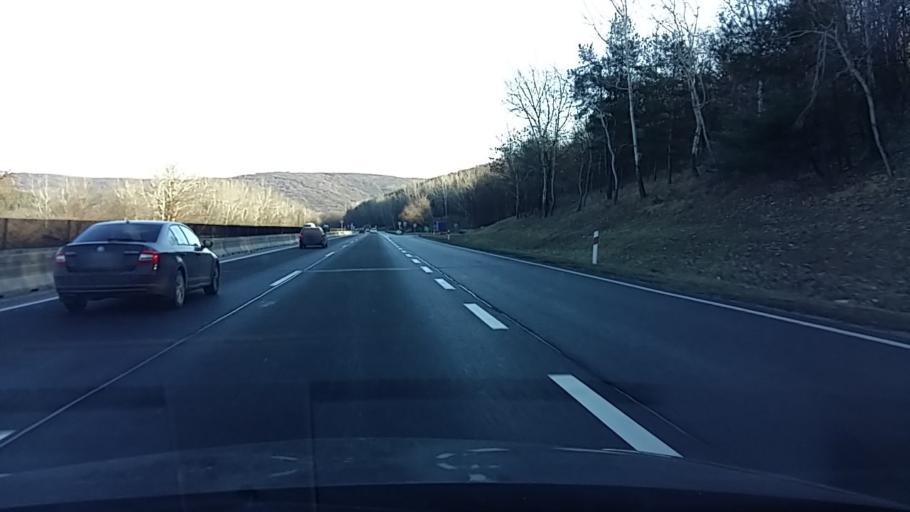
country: HU
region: Pest
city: Godollo
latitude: 47.6127
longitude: 19.3889
